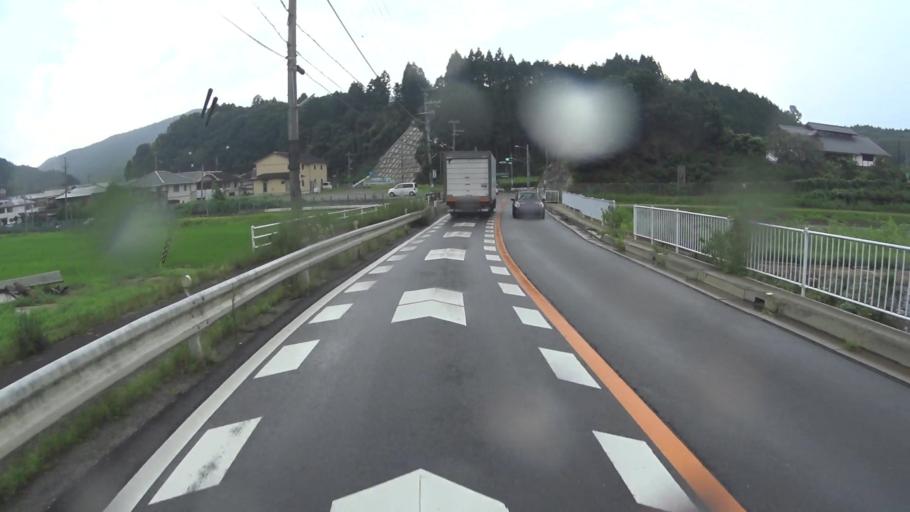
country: JP
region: Kyoto
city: Uji
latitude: 34.8586
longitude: 135.8813
